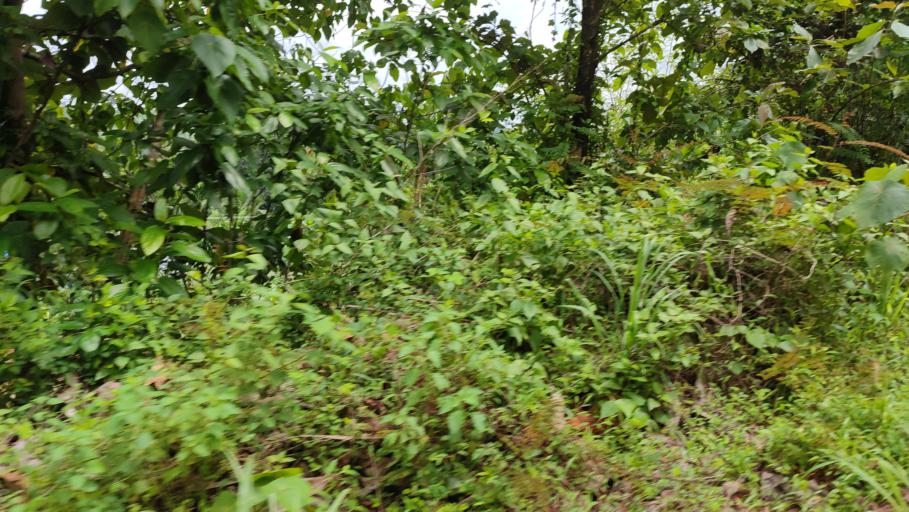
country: IN
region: Kerala
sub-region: Kasaragod District
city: Nileshwar
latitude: 12.2844
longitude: 75.2607
